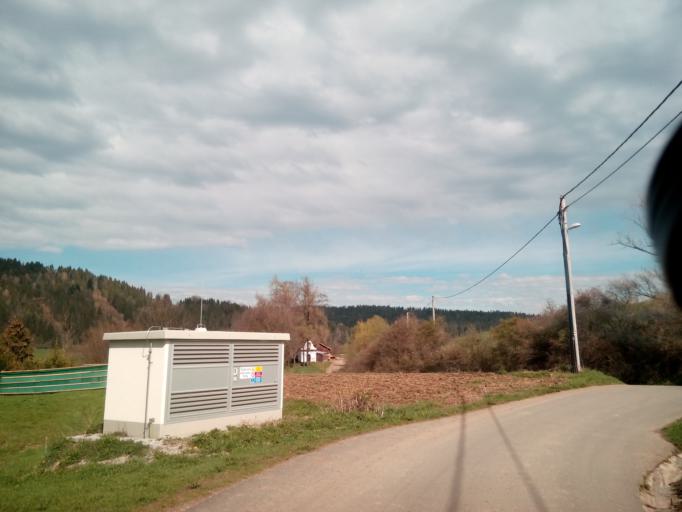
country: PL
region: Lesser Poland Voivodeship
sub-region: Powiat nowotarski
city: Niedzica
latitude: 49.3410
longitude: 20.2877
